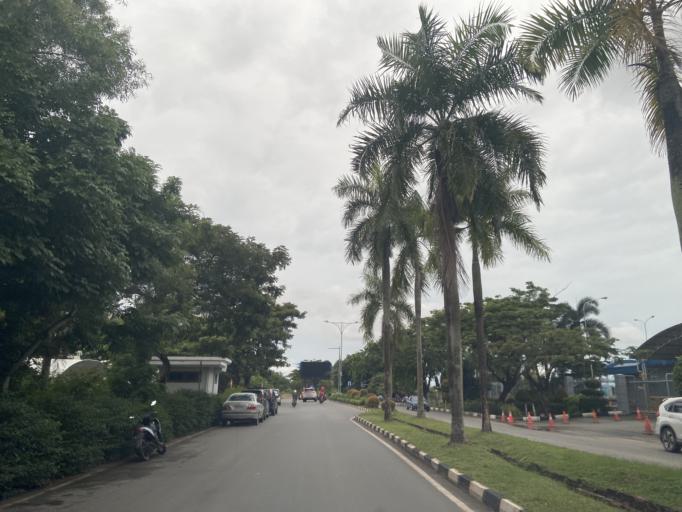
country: SG
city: Singapore
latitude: 1.1301
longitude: 104.0559
